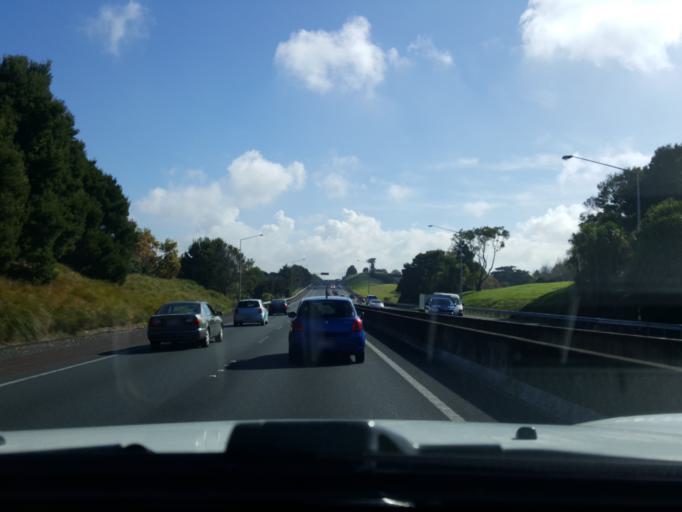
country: NZ
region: Auckland
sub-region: Auckland
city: Wiri
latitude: -36.9893
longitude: 174.8380
